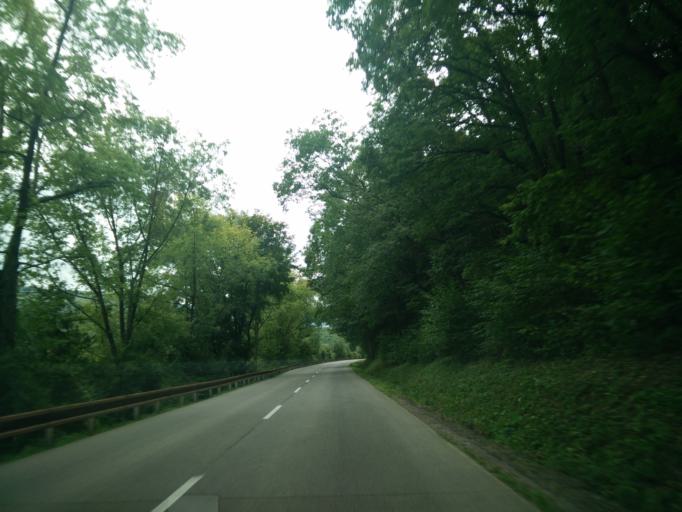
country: SK
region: Nitriansky
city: Novaky
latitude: 48.5998
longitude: 18.5045
